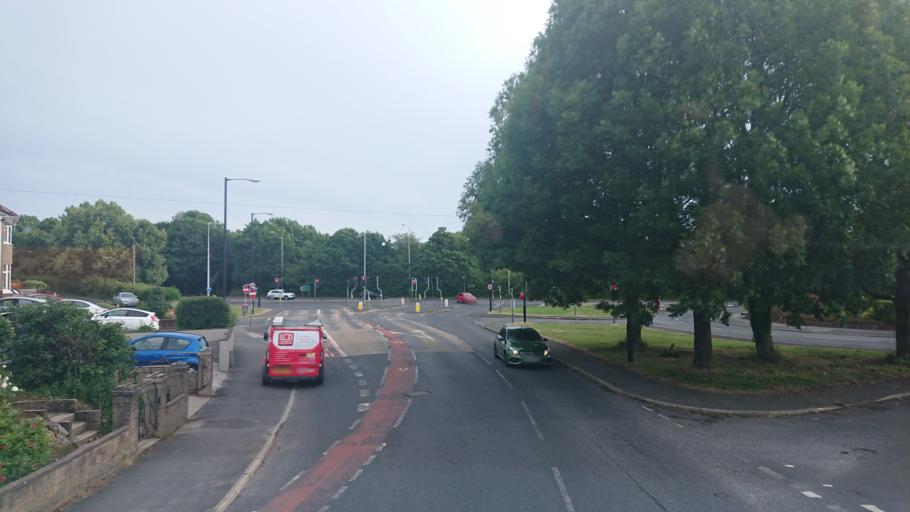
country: GB
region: England
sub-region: Lancashire
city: Lancaster
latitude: 54.0569
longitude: -2.8169
